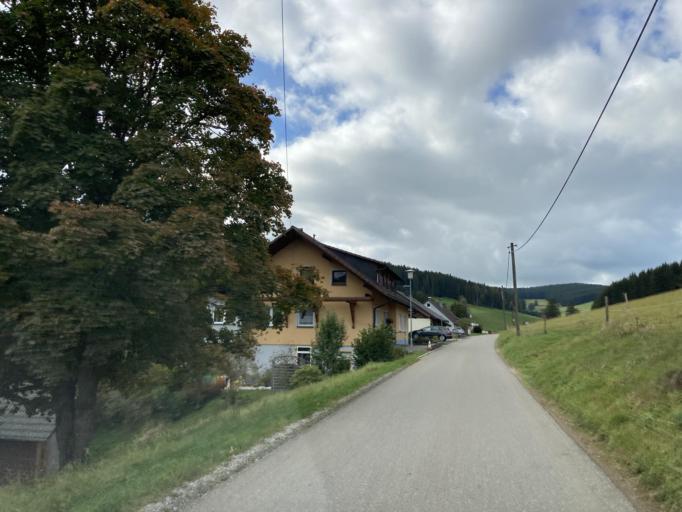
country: DE
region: Baden-Wuerttemberg
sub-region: Freiburg Region
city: Vohrenbach
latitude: 48.0547
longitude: 8.2978
